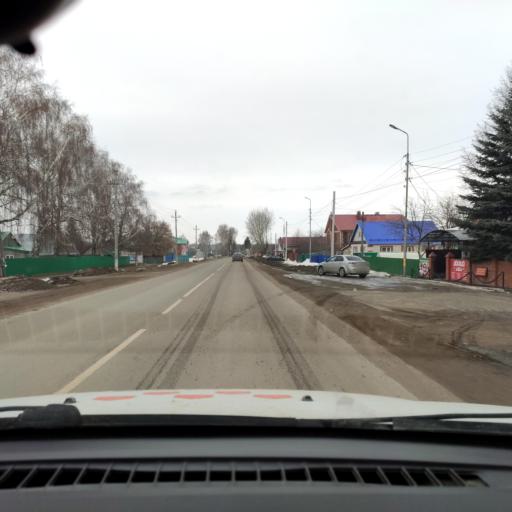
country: RU
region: Bashkortostan
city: Kushnarenkovo
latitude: 55.1031
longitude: 55.3405
